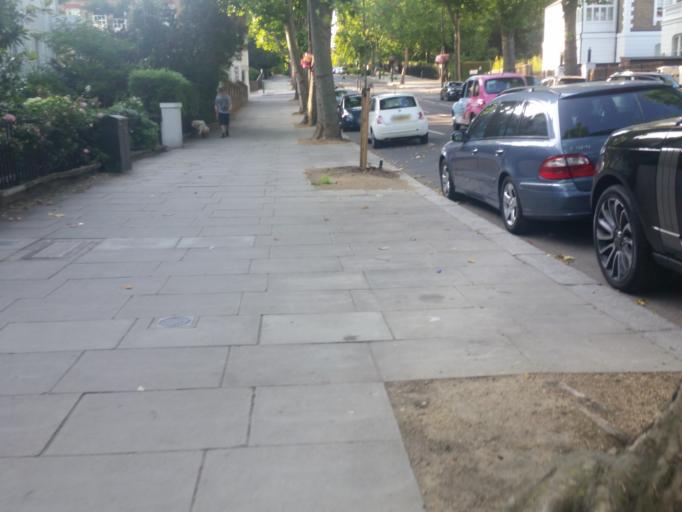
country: GB
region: England
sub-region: Greater London
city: Kensington
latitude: 51.5090
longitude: -0.2039
